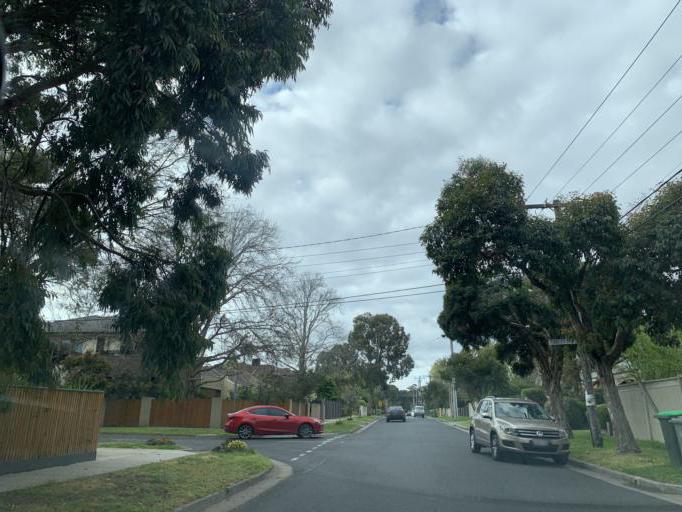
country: AU
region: Victoria
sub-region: Bayside
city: Cheltenham
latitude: -37.9730
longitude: 145.0394
